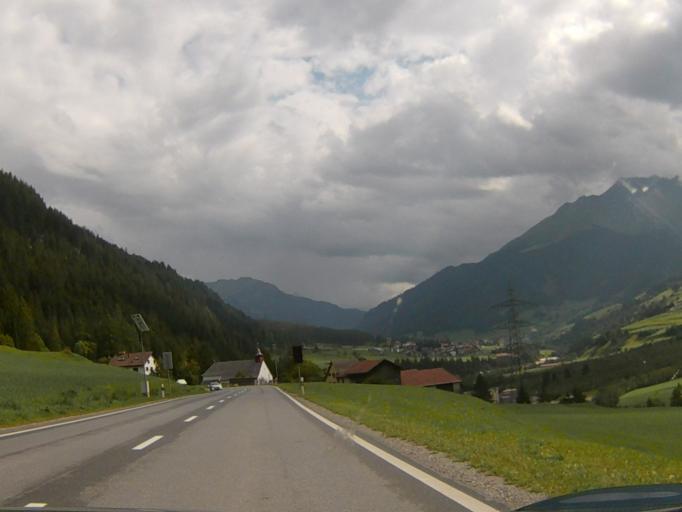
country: CH
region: Grisons
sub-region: Albula District
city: Tiefencastel
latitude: 46.6263
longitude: 9.5855
